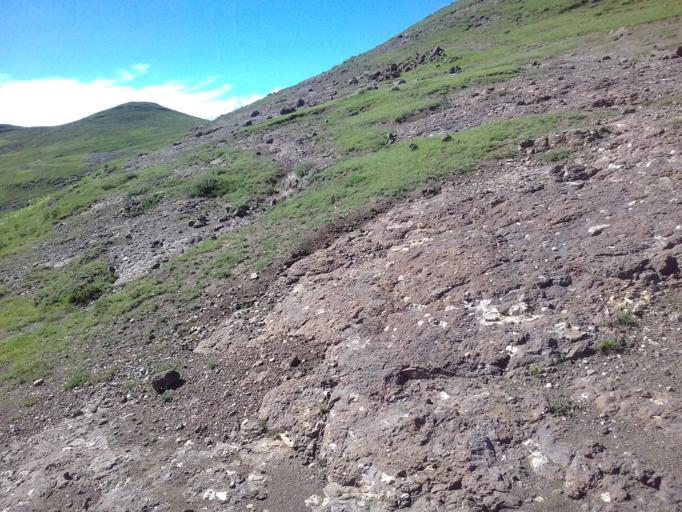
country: LS
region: Thaba-Tseka
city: Thaba-Tseka
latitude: -29.5253
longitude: 28.5835
